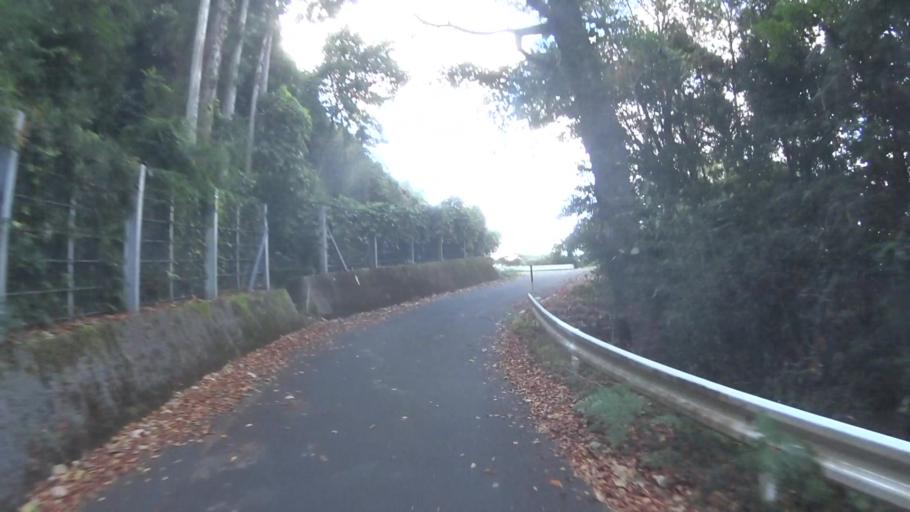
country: JP
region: Kyoto
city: Maizuru
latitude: 35.5671
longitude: 135.4193
